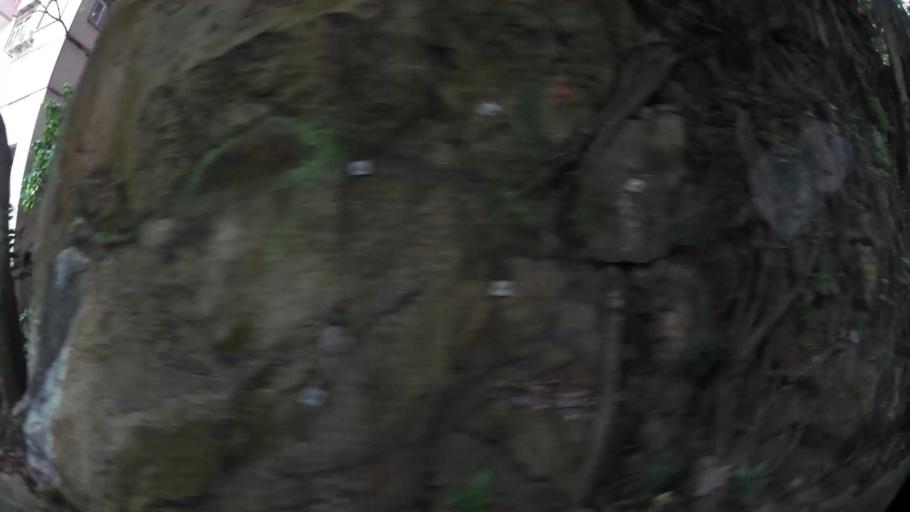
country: HK
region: Wanchai
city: Wan Chai
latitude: 22.2762
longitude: 114.1925
